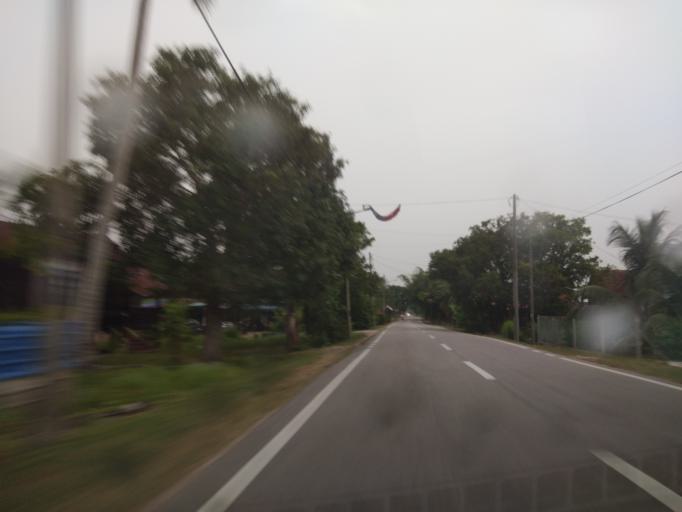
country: MY
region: Penang
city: Kepala Batas
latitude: 5.4979
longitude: 100.3965
